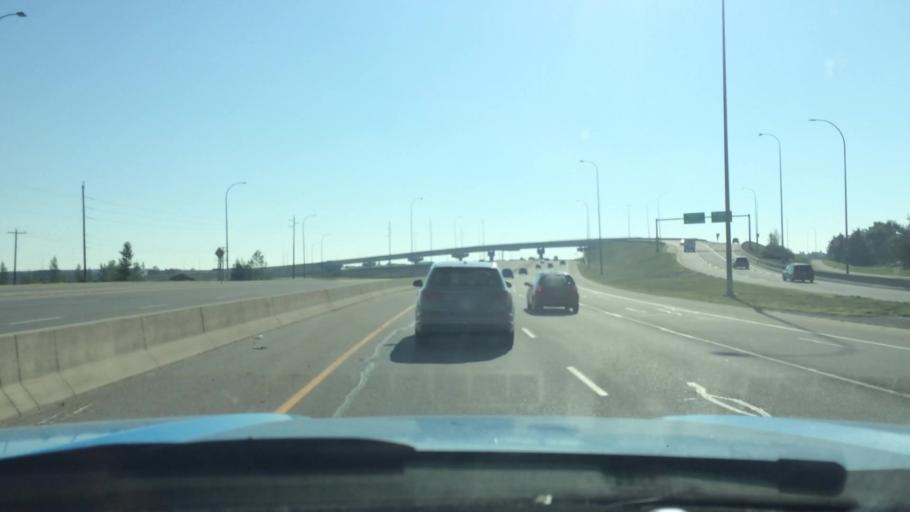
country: CA
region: Alberta
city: Calgary
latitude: 51.0955
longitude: -113.9892
